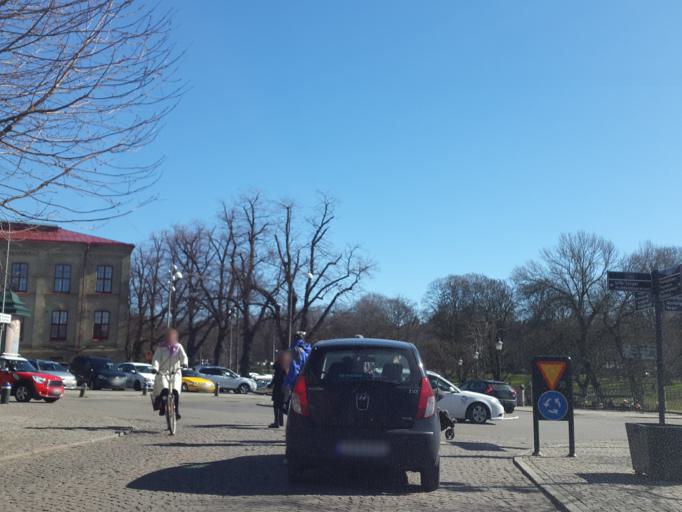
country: SE
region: Vaestra Goetaland
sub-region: Goteborg
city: Goeteborg
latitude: 57.7009
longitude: 11.9605
